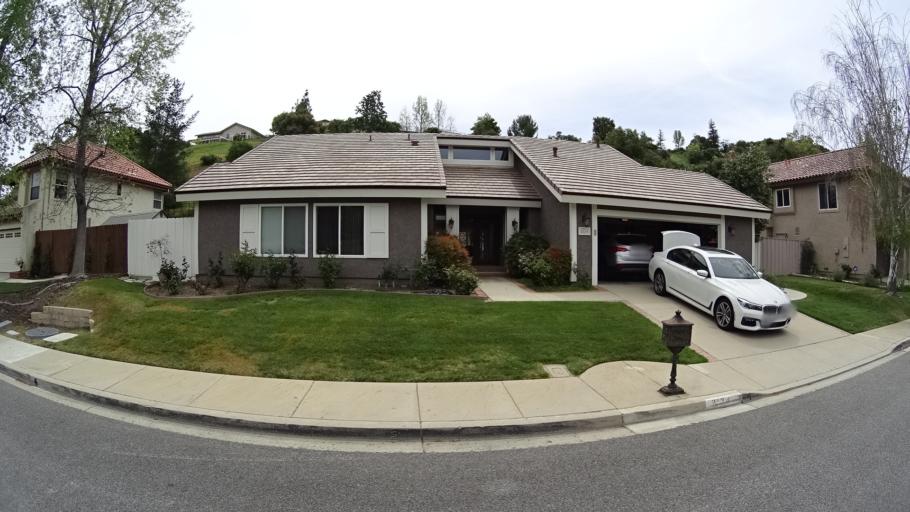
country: US
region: California
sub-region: Ventura County
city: Thousand Oaks
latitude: 34.1435
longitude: -118.8406
